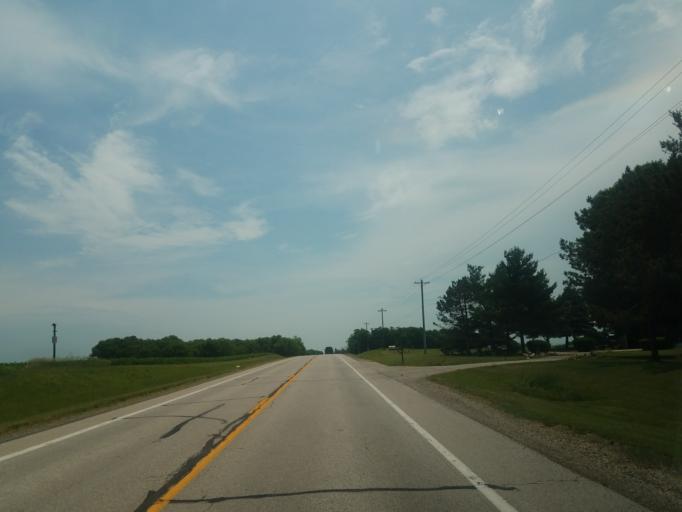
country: US
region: Illinois
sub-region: McLean County
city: Bloomington
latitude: 40.4414
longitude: -88.9429
